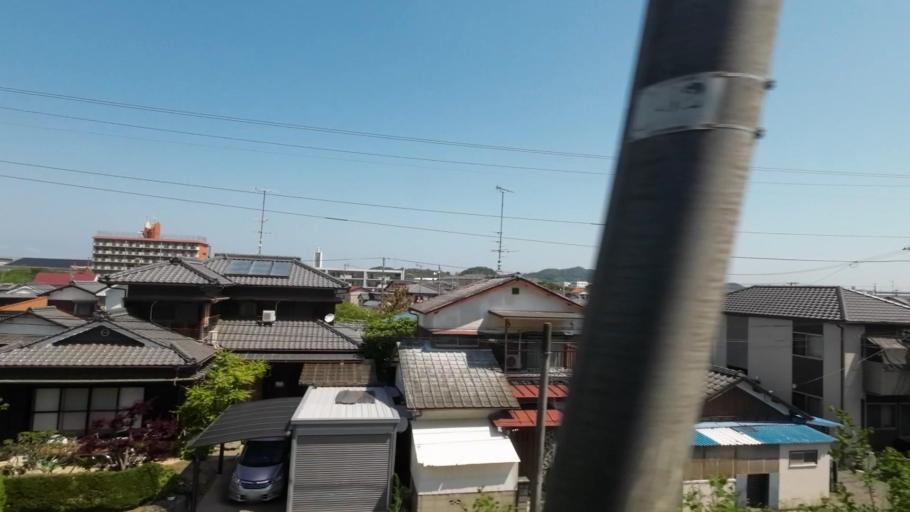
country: JP
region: Ehime
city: Niihama
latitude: 33.9737
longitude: 133.3431
